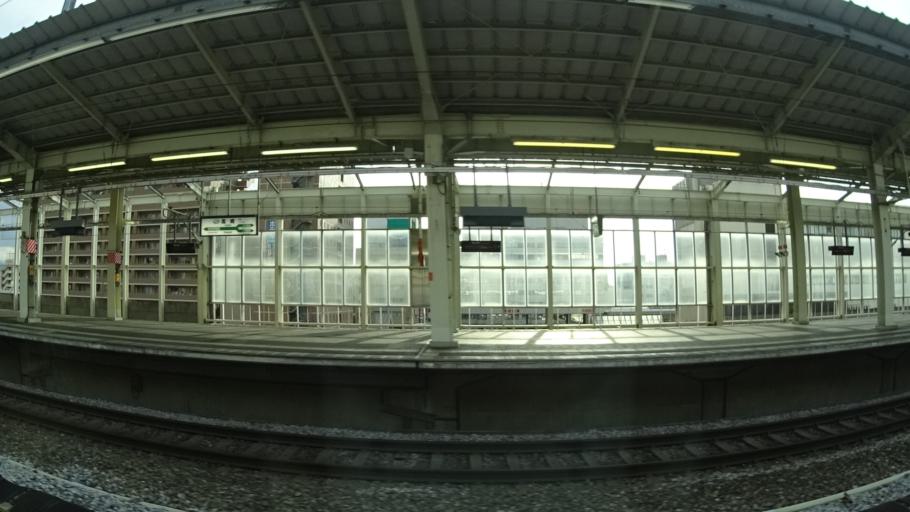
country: JP
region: Gunma
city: Takasaki
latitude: 36.3223
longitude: 139.0130
